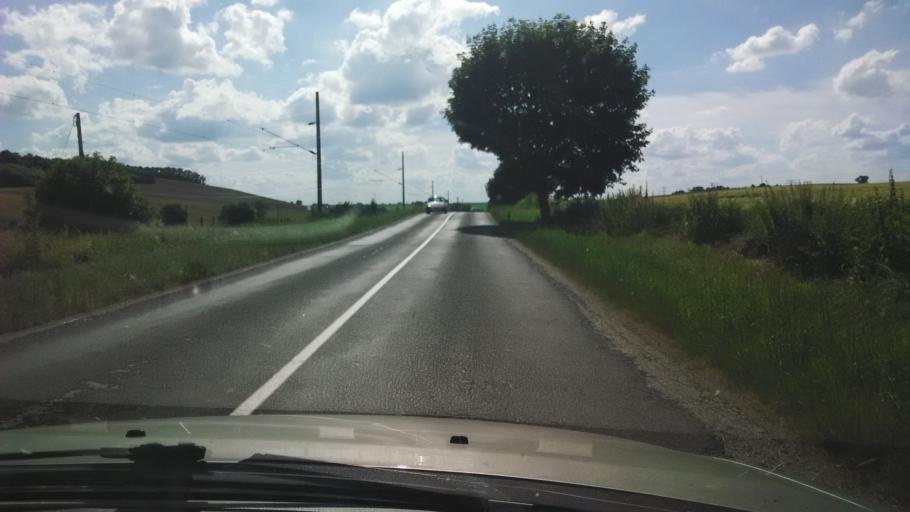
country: SK
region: Nitriansky
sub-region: Okres Nitra
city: Vrable
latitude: 48.1168
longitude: 18.3762
